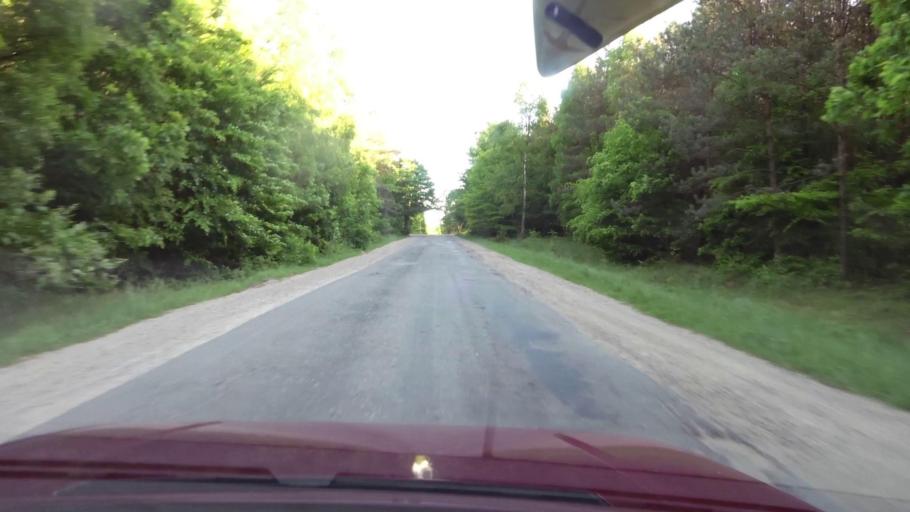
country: PL
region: West Pomeranian Voivodeship
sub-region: Powiat szczecinecki
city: Bialy Bor
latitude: 53.9238
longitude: 16.8041
